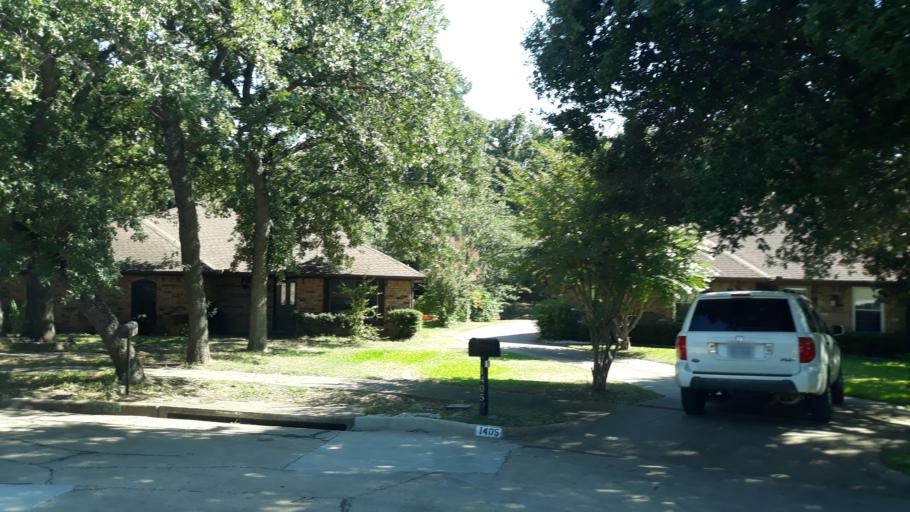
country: US
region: Texas
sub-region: Dallas County
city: Irving
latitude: 32.8291
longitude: -97.0027
